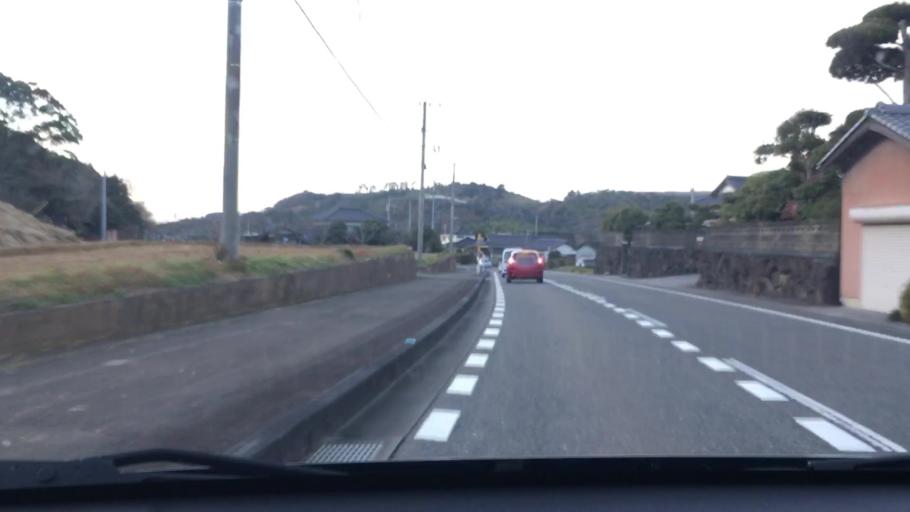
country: JP
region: Oita
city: Bungo-Takada-shi
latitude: 33.4998
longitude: 131.3754
